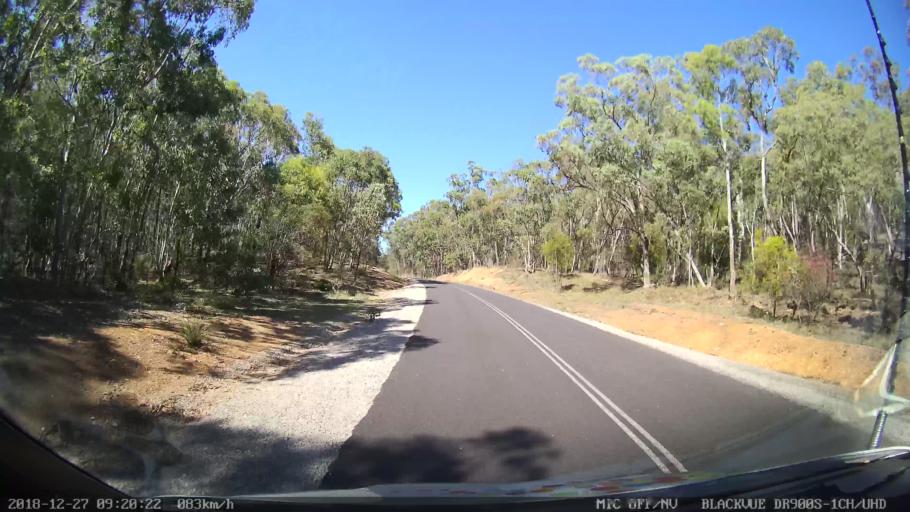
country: AU
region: New South Wales
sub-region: Lithgow
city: Portland
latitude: -33.1189
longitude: 150.0234
